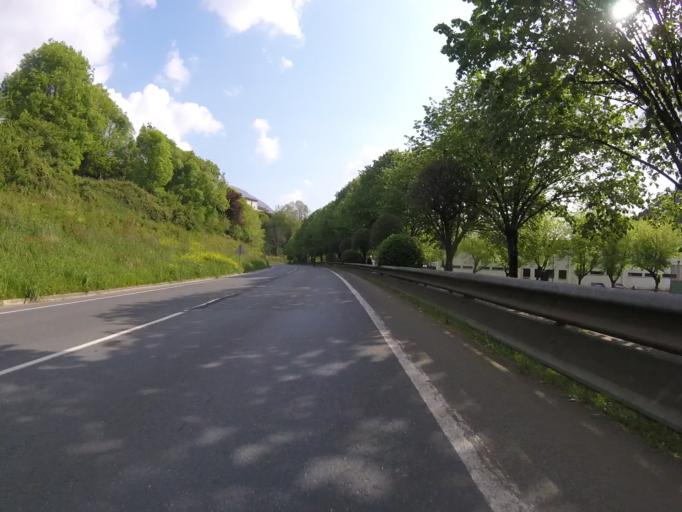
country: ES
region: Basque Country
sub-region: Provincia de Guipuzcoa
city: Azkoitia
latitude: 43.1737
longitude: -2.3013
